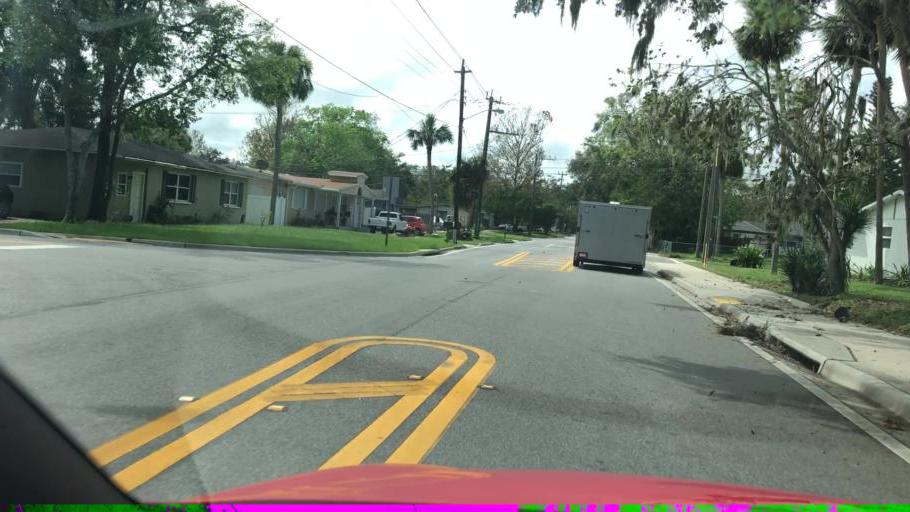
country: US
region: Florida
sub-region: Volusia County
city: Ormond Beach
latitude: 29.2696
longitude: -81.0617
